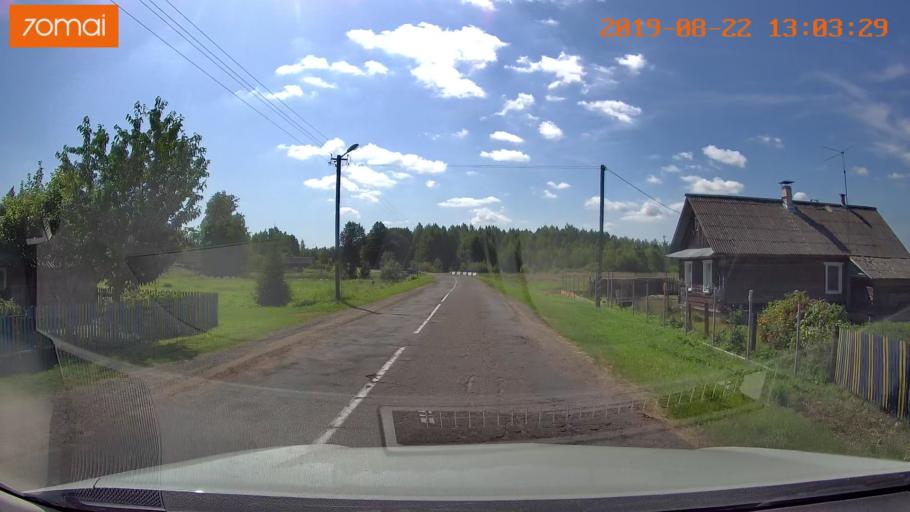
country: BY
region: Minsk
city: Prawdzinski
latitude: 53.3799
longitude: 27.8203
